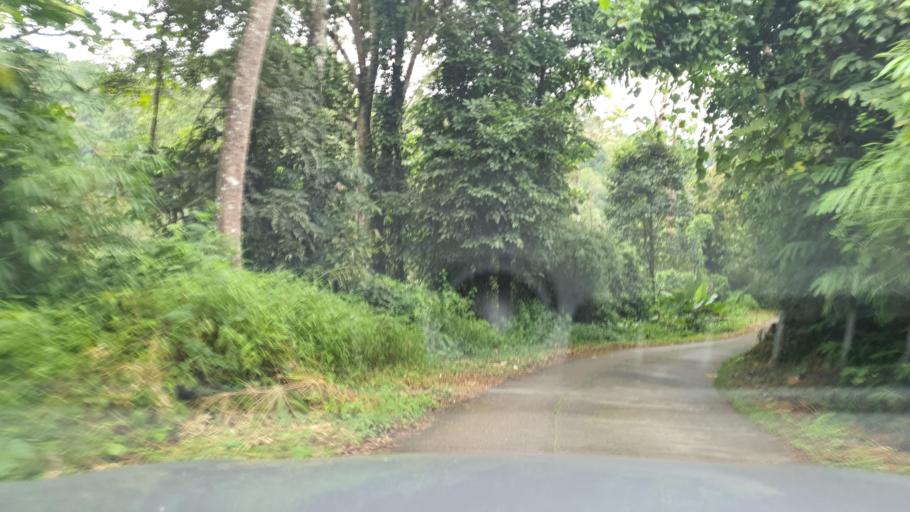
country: TH
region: Chiang Mai
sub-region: Amphoe Chiang Dao
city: Chiang Dao
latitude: 19.2710
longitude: 98.9326
